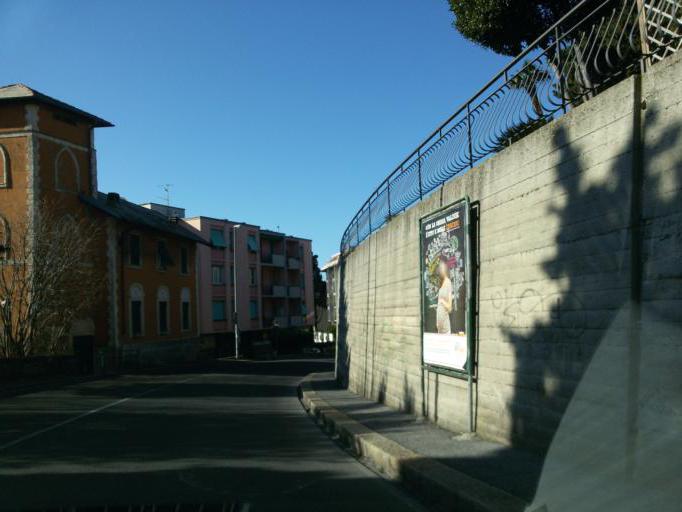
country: IT
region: Liguria
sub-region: Provincia di Genova
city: Genoa
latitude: 44.4005
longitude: 8.9796
